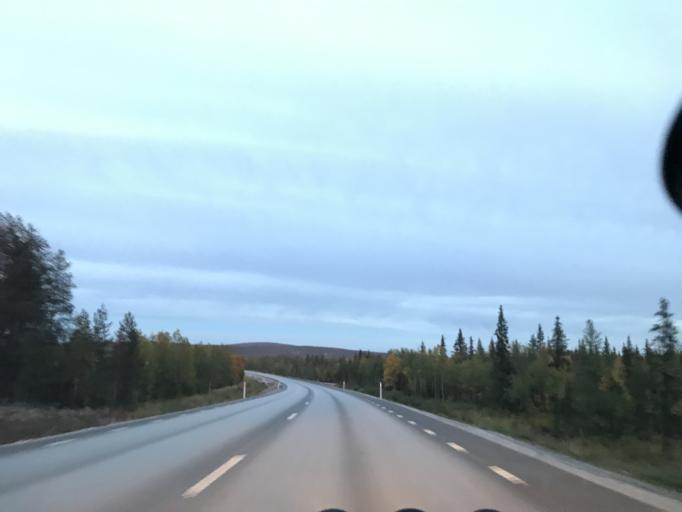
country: SE
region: Norrbotten
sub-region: Gallivare Kommun
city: Malmberget
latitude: 67.6480
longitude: 21.0253
